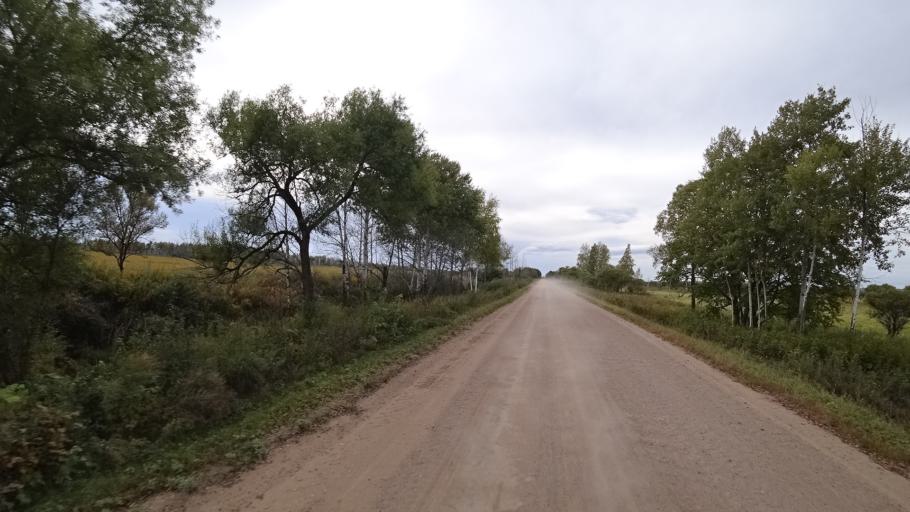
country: RU
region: Amur
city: Arkhara
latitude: 49.3737
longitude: 130.2028
